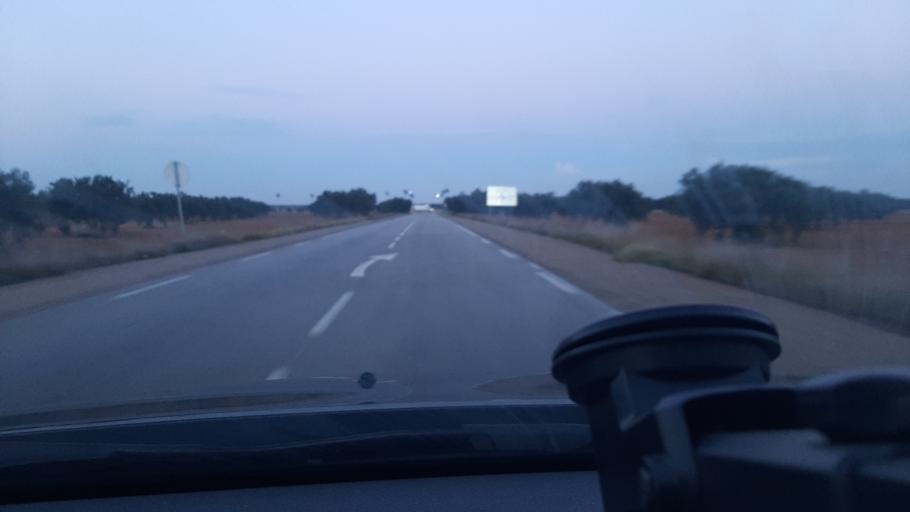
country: TN
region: Al Mahdiyah
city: Shurban
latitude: 35.0377
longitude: 10.5228
